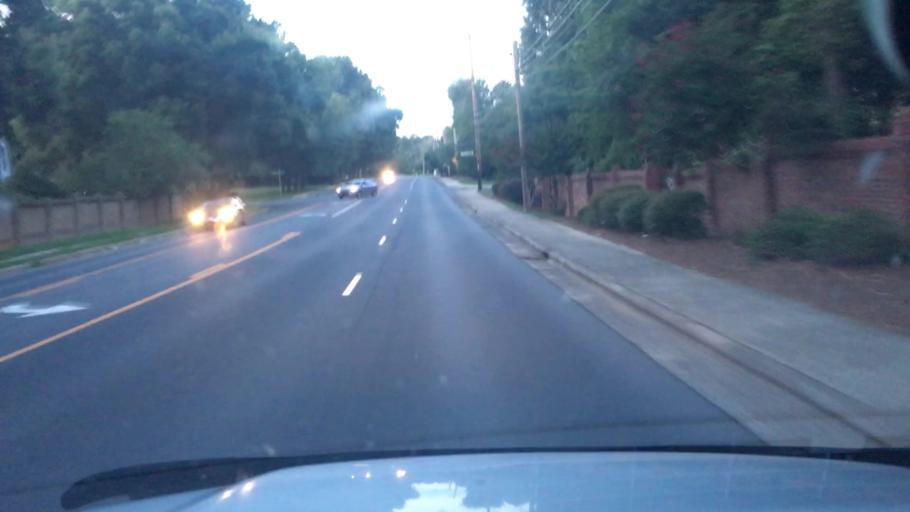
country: US
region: North Carolina
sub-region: Mecklenburg County
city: Pineville
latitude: 35.1185
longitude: -80.8214
